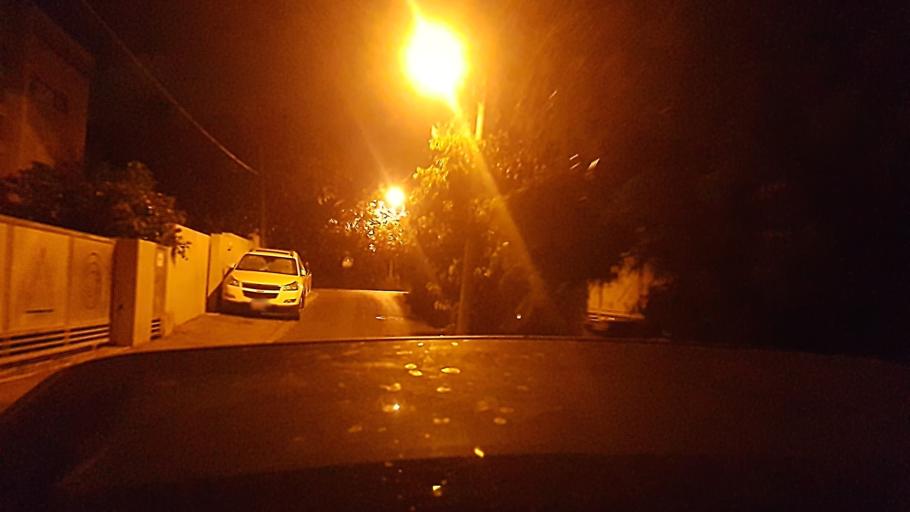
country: IL
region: Central District
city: Hod HaSharon
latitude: 32.1637
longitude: 34.8760
